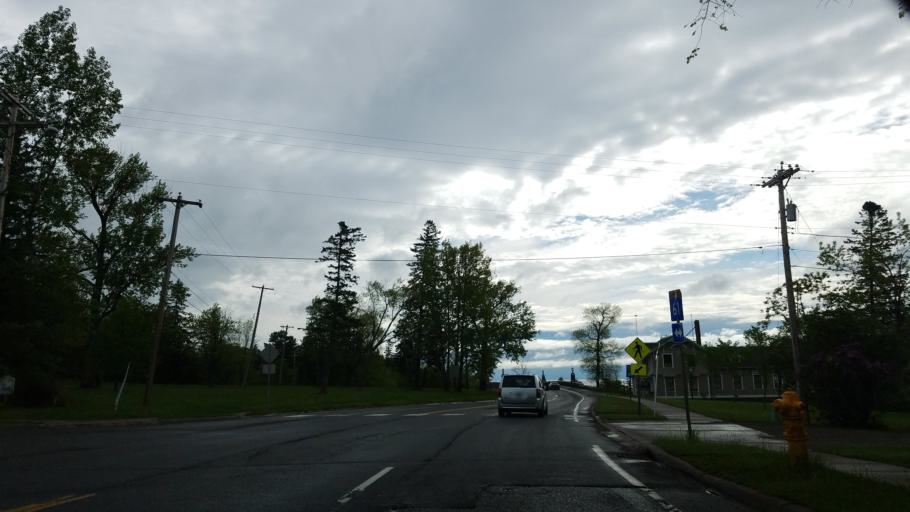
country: US
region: Minnesota
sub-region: Saint Louis County
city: Arnold
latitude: 46.8365
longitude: -92.0087
